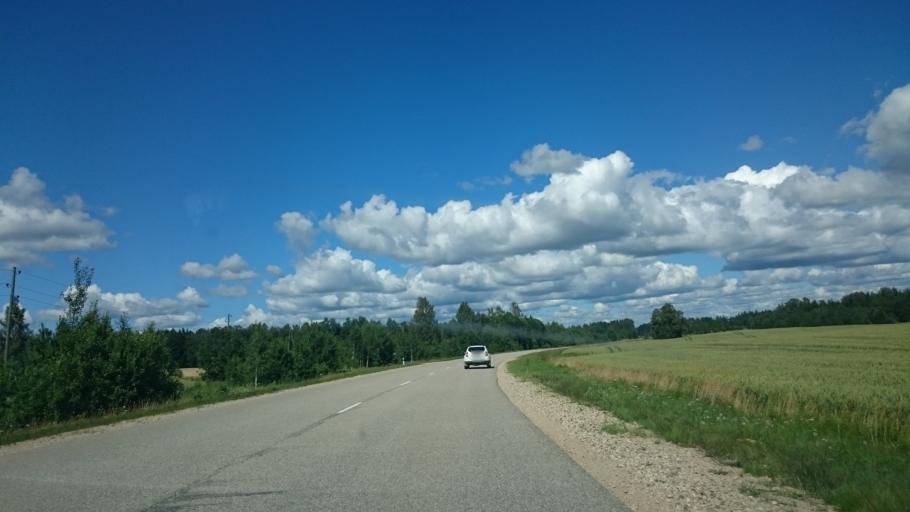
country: LV
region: Kuldigas Rajons
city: Kuldiga
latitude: 56.9004
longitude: 21.8902
